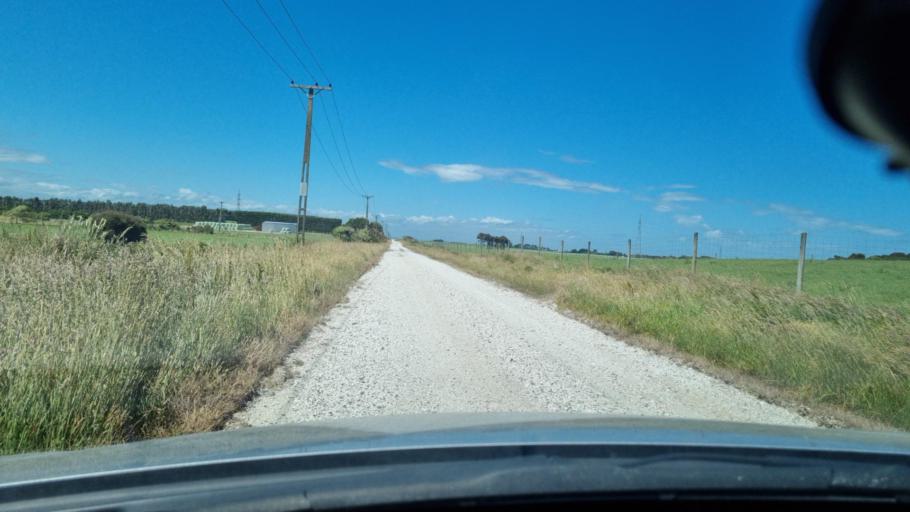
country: NZ
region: Southland
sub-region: Invercargill City
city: Invercargill
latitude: -46.4426
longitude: 168.4325
